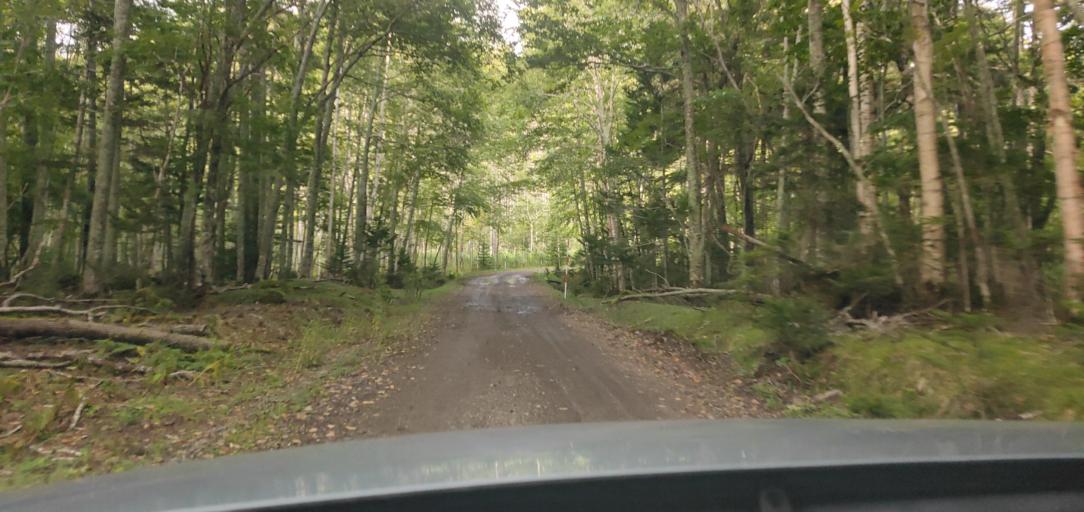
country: JP
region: Hokkaido
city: Kitami
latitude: 43.3741
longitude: 143.9615
